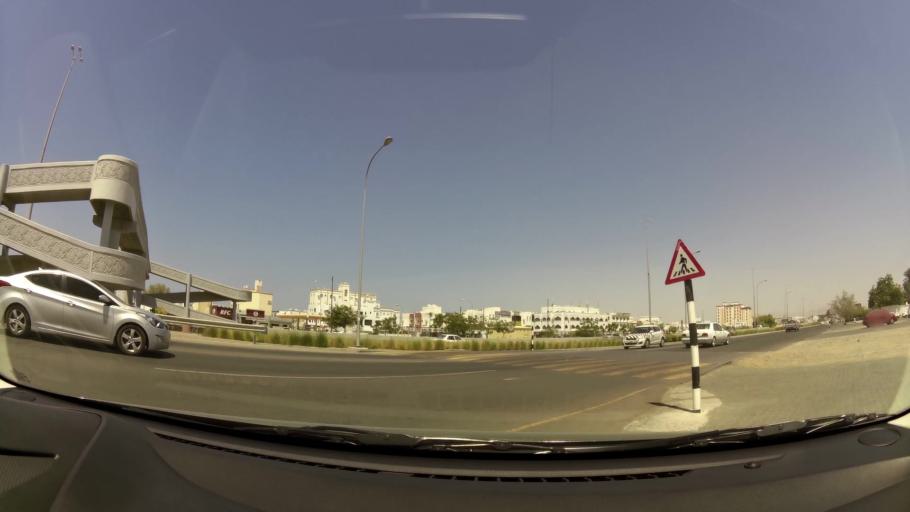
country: OM
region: Muhafazat Masqat
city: As Sib al Jadidah
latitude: 23.6331
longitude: 58.2301
